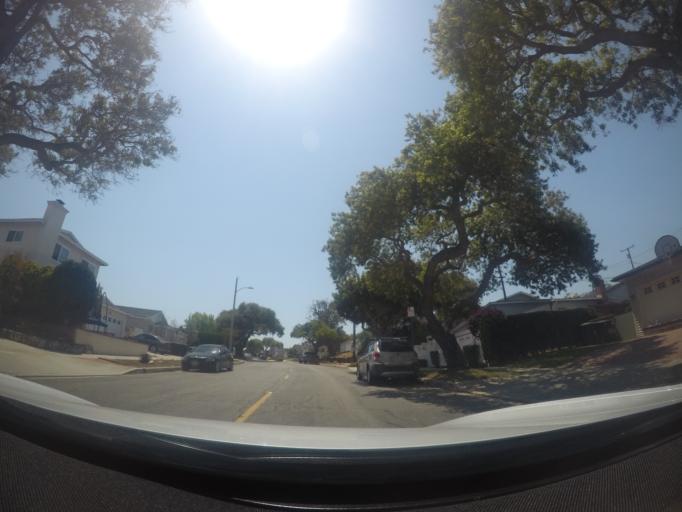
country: US
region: California
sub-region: Los Angeles County
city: Torrance
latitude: 33.8186
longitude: -118.3627
